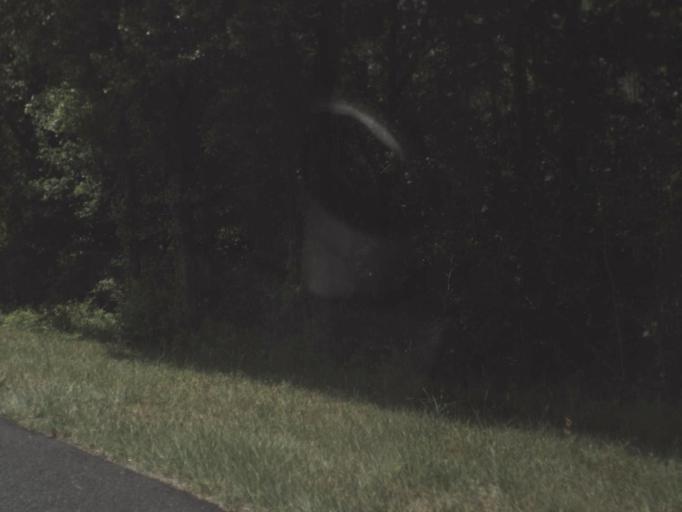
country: US
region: Florida
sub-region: Taylor County
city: Perry
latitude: 30.2202
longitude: -83.6730
